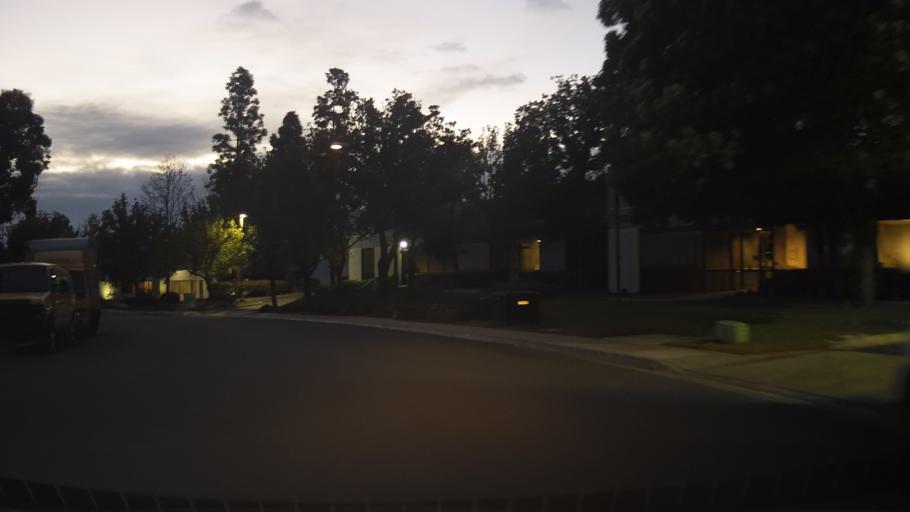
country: US
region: California
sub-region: San Diego County
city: National City
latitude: 32.7149
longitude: -117.1129
